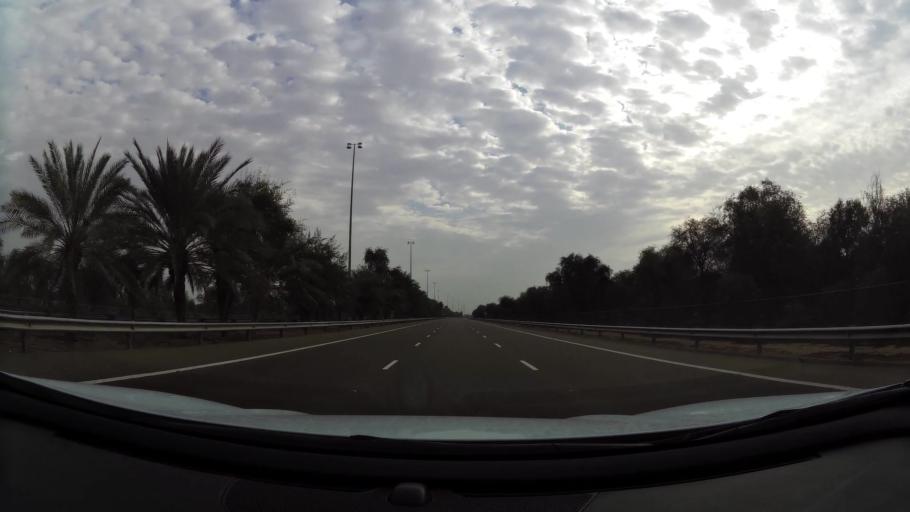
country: AE
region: Abu Dhabi
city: Al Ain
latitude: 24.1737
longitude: 55.2945
